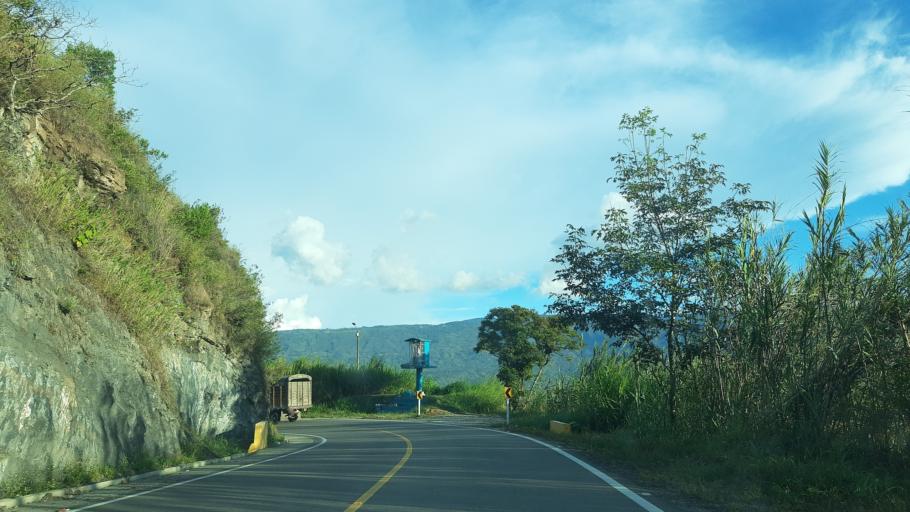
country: CO
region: Boyaca
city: Guateque
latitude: 5.0021
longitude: -73.5062
